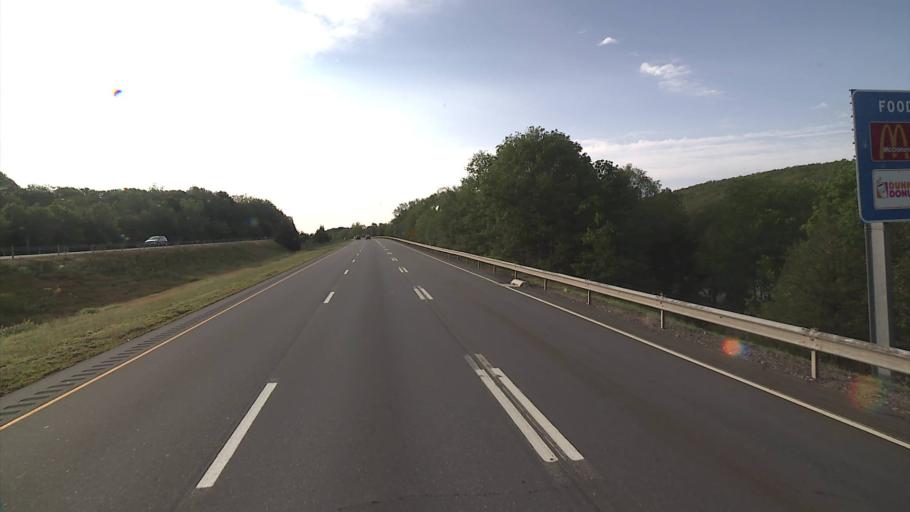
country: US
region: Connecticut
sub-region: New London County
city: Colchester
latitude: 41.5761
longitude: -72.3500
